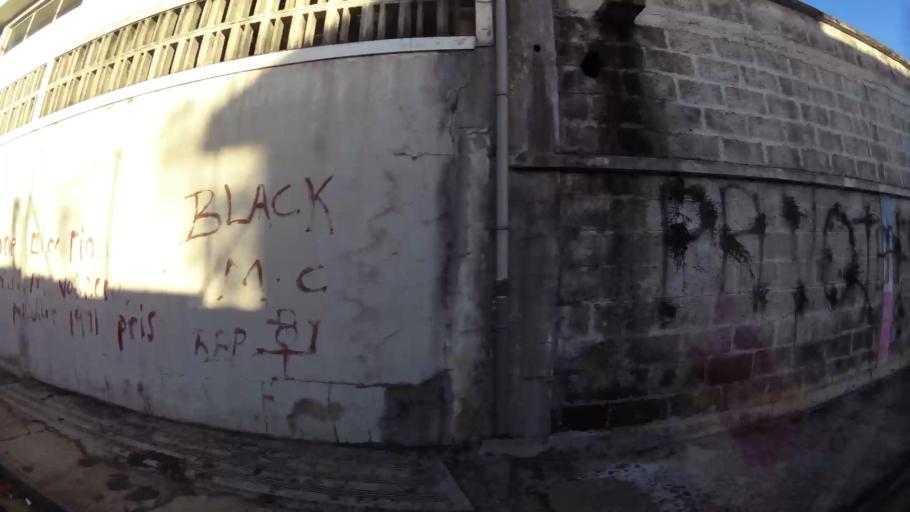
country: MU
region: Port Louis
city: Port Louis
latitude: -20.1725
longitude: 57.5051
